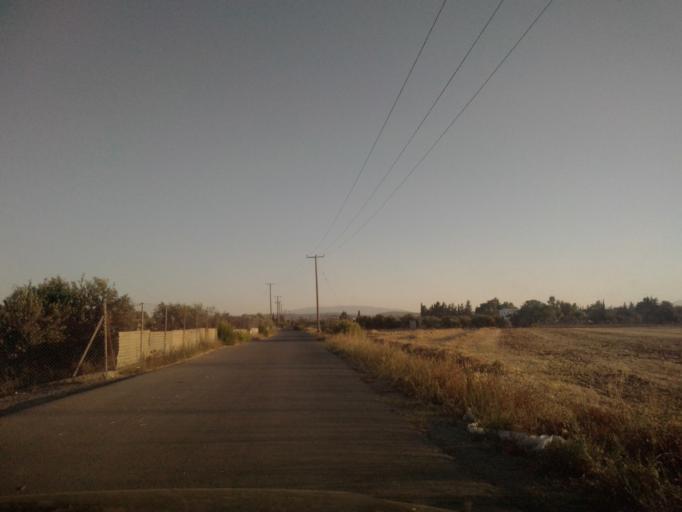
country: CY
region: Limassol
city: Ypsonas
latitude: 34.6725
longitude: 32.9639
